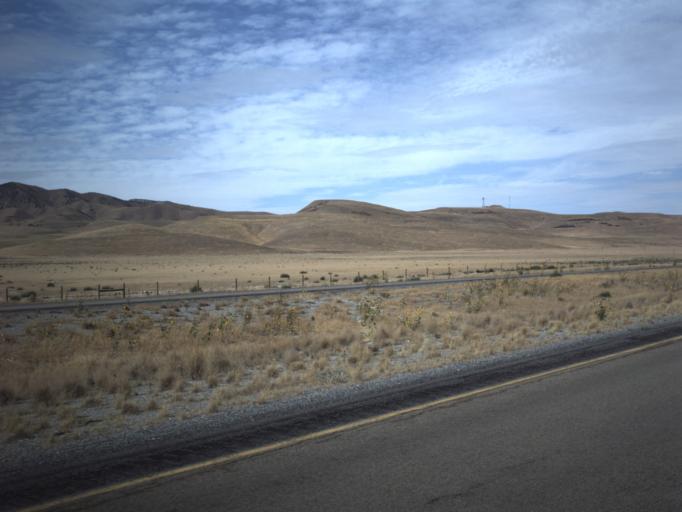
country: US
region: Utah
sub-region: Tooele County
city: Grantsville
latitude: 40.7948
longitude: -112.8395
